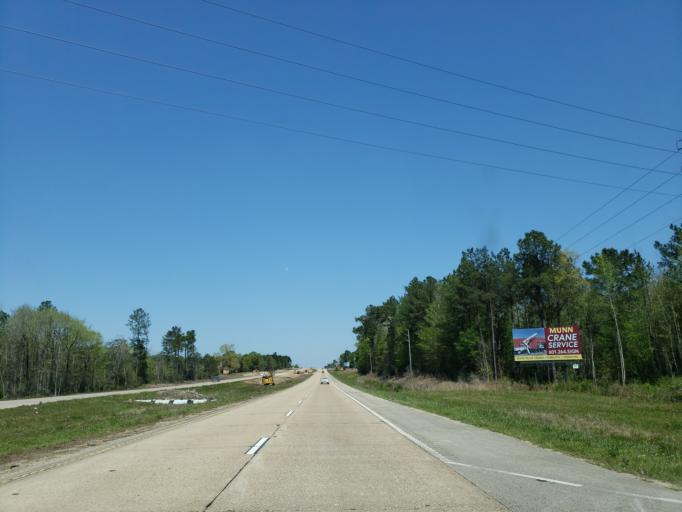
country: US
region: Mississippi
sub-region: Stone County
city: Wiggins
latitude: 31.0586
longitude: -89.2065
